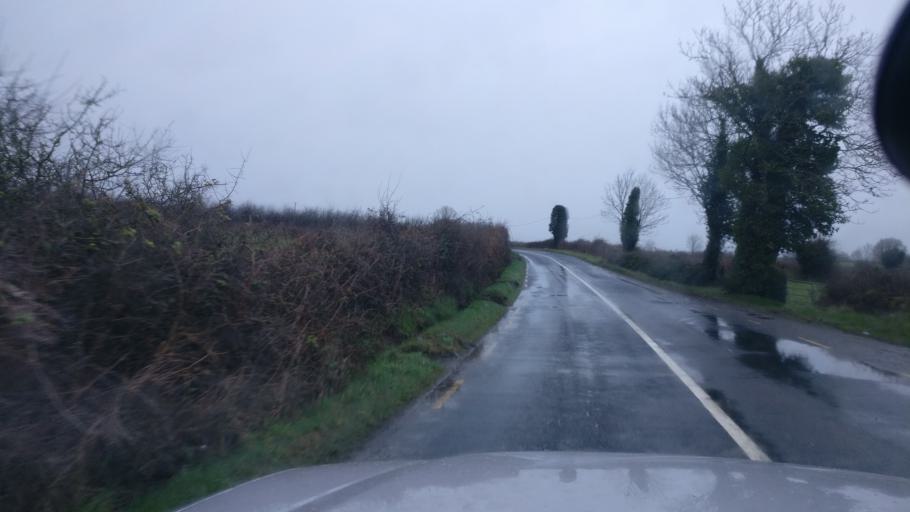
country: IE
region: Connaught
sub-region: County Galway
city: Loughrea
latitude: 53.0978
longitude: -8.4270
